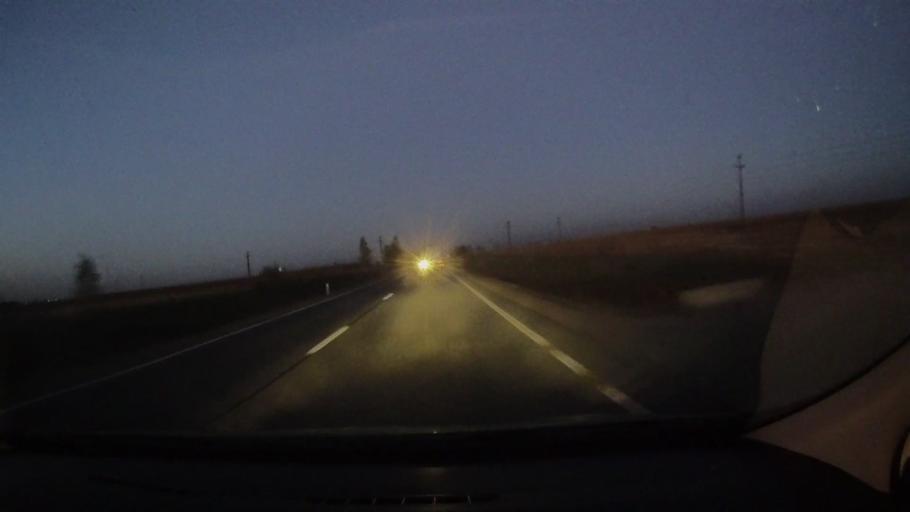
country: RO
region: Bihor
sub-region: Comuna Curtuiuseni
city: Curtuiseni
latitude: 47.5309
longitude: 22.1945
